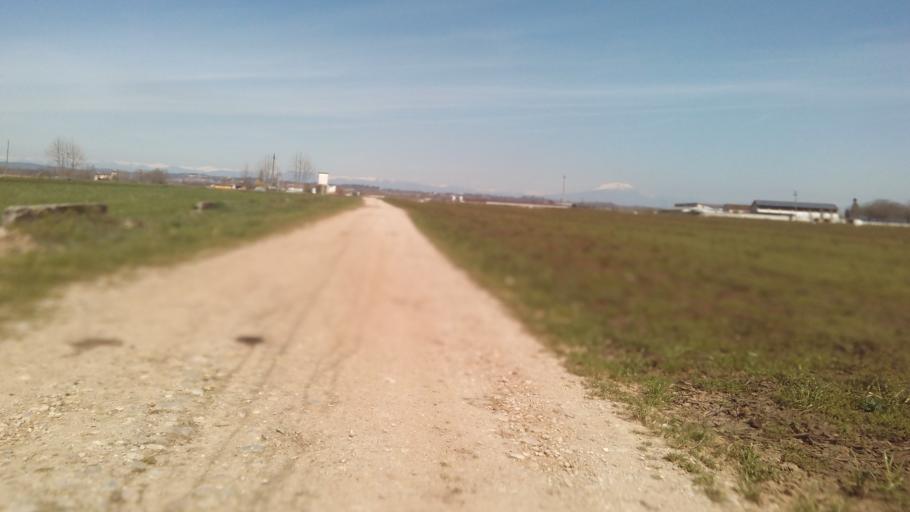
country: IT
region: Lombardy
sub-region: Provincia di Mantova
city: Cerlongo
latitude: 45.2756
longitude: 10.6699
